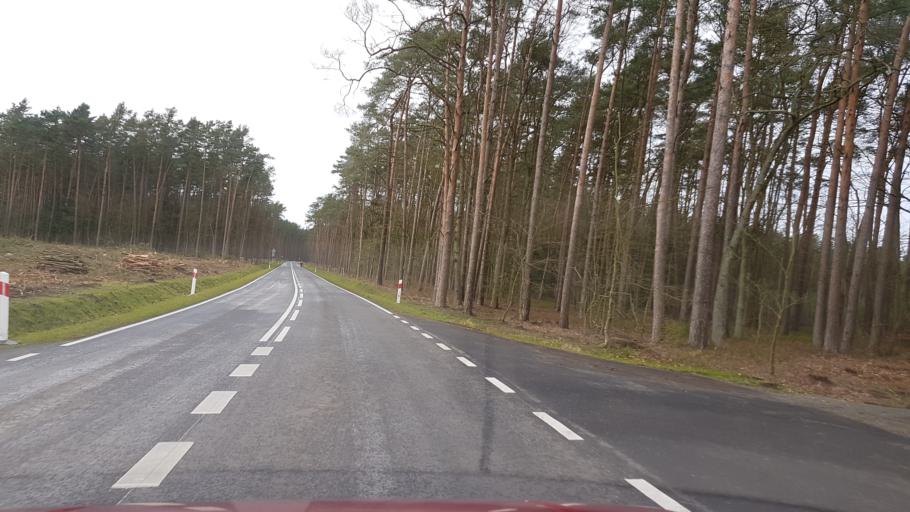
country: PL
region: West Pomeranian Voivodeship
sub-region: Powiat policki
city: Police
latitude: 53.6555
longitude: 14.4778
